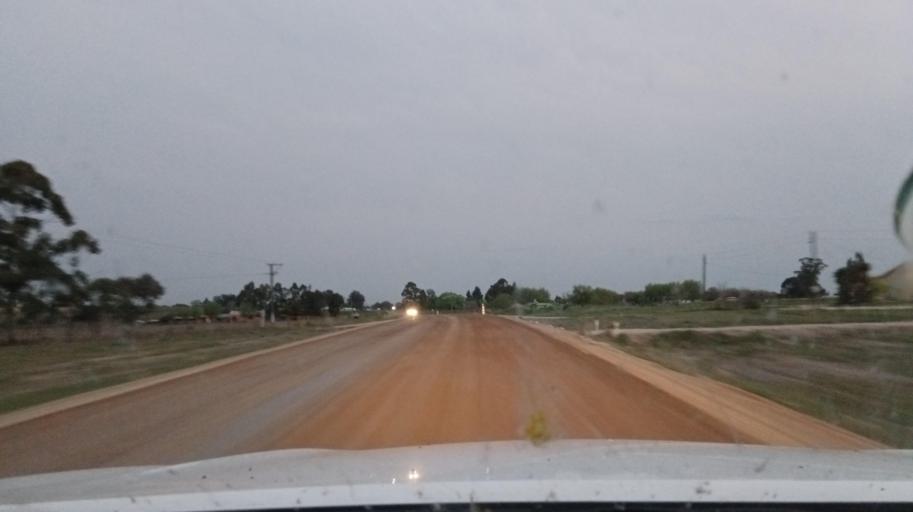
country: UY
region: Canelones
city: Santa Rosa
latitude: -34.5461
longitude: -56.1016
